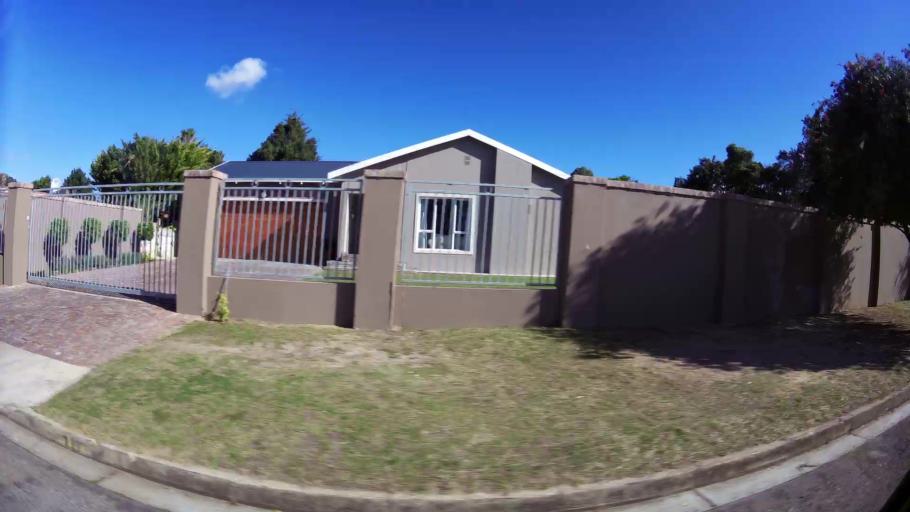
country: ZA
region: Western Cape
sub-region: Eden District Municipality
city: George
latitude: -33.9563
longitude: 22.4295
